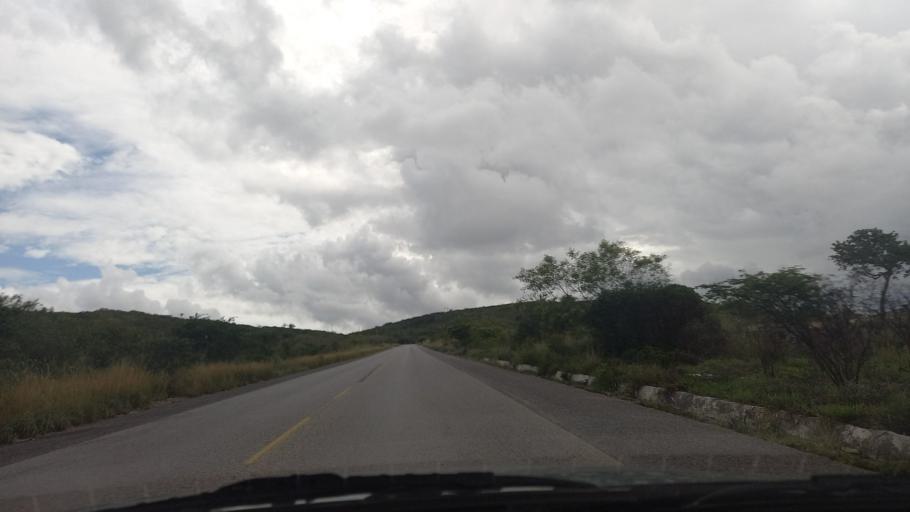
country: BR
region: Pernambuco
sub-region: Lajedo
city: Lajedo
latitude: -8.6727
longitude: -36.3937
